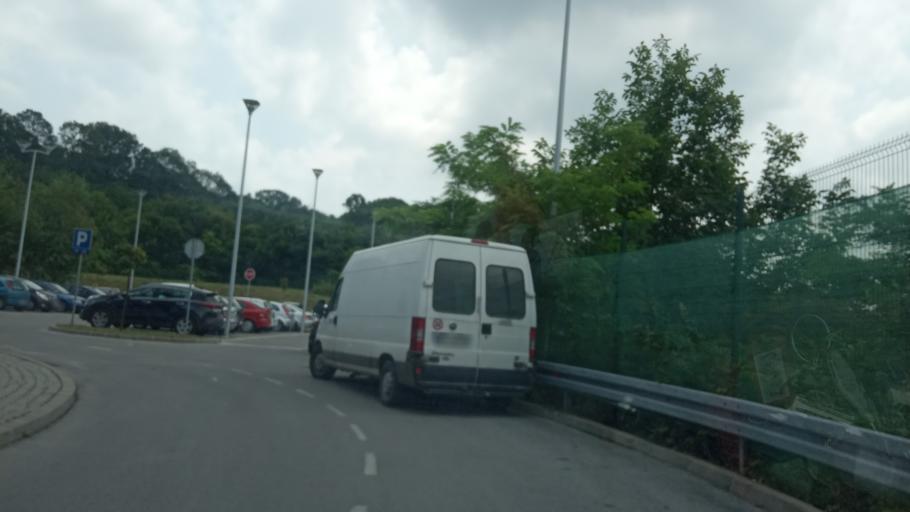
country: RS
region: Central Serbia
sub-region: Belgrade
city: Palilula
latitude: 44.8031
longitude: 20.5026
